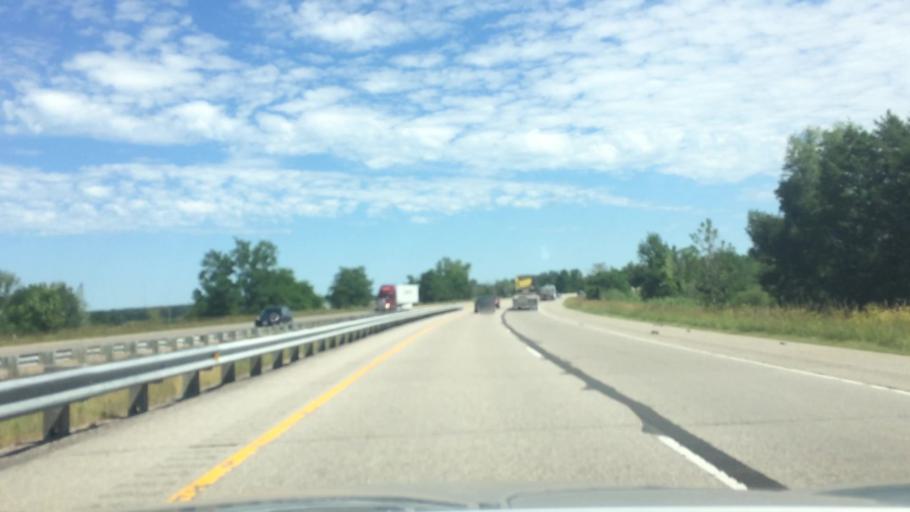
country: US
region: Wisconsin
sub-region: Marquette County
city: Westfield
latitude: 43.7334
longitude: -89.4848
